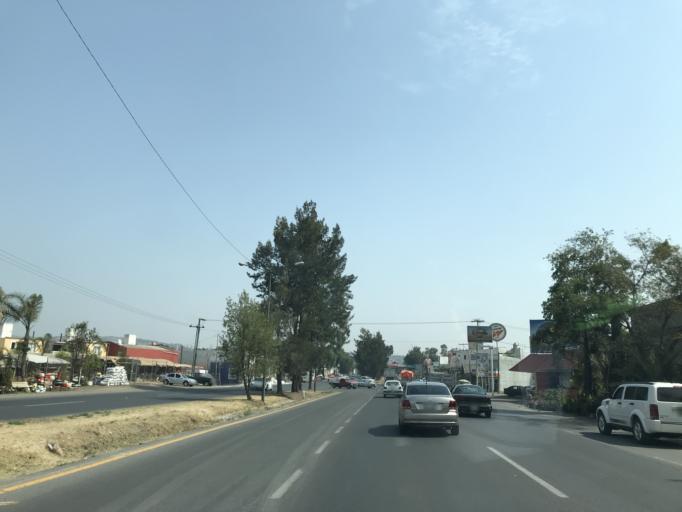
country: MX
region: Tlaxcala
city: Tlaxcala de Xicohtencatl
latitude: 19.3256
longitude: -98.2004
